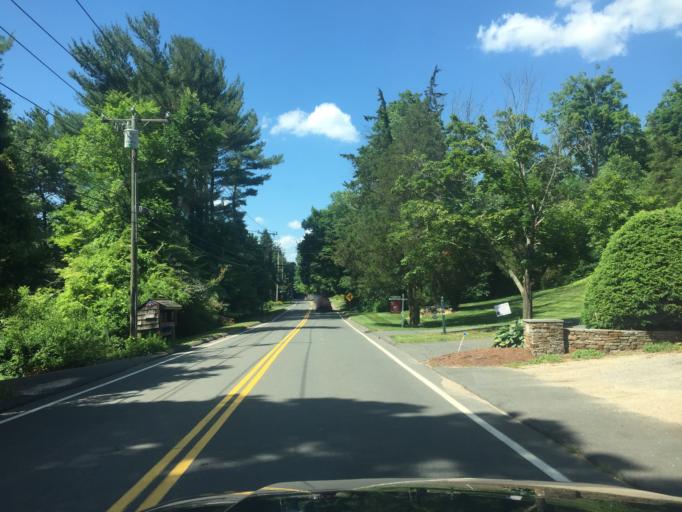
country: US
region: Connecticut
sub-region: Hartford County
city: Farmington
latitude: 41.7520
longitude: -72.8151
